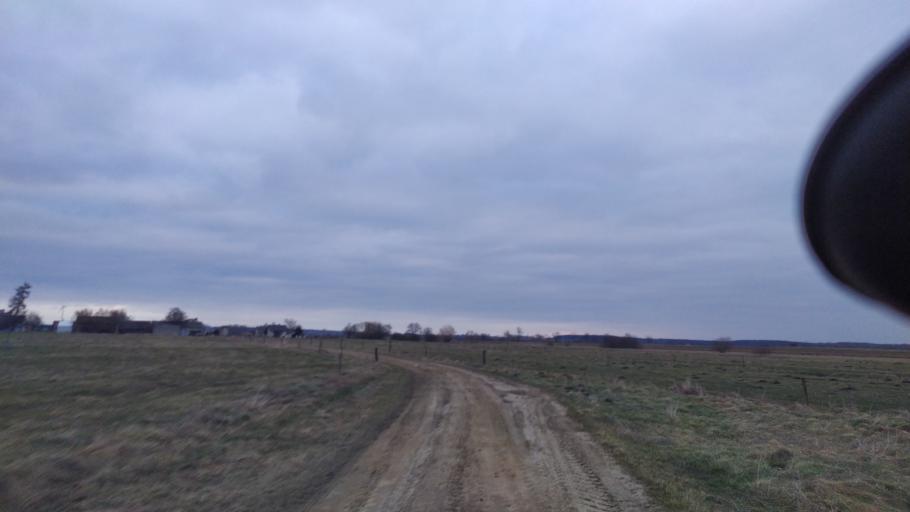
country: PL
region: Lublin Voivodeship
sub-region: Powiat lubartowski
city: Abramow
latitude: 51.4372
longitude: 22.2942
